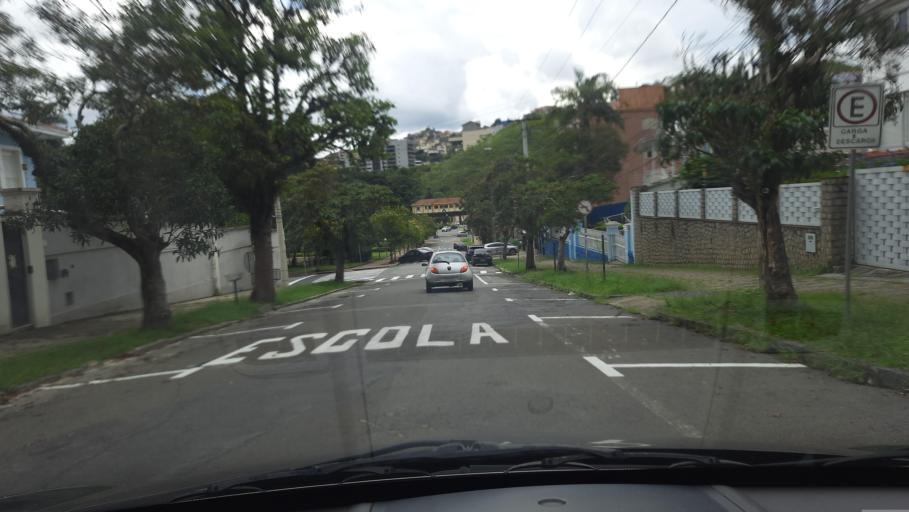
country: BR
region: Minas Gerais
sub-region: Pocos De Caldas
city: Pocos de Caldas
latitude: -21.7840
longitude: -46.5716
